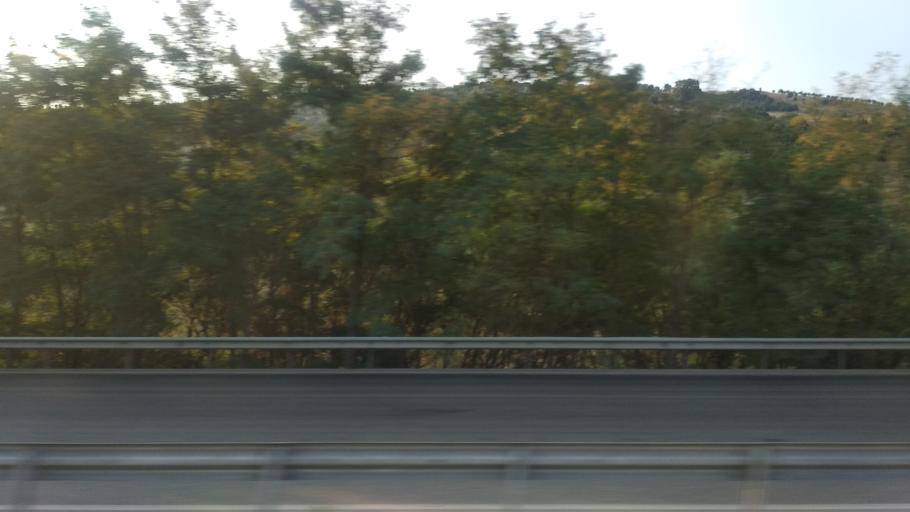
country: TR
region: Manisa
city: Menye
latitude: 38.5496
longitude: 28.4580
